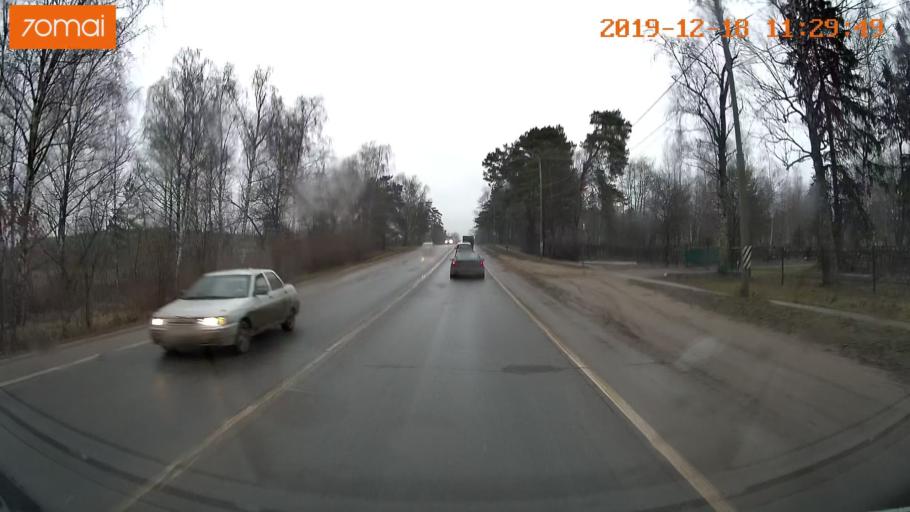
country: RU
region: Moskovskaya
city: Bol'shiye Vyazemy
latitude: 55.6522
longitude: 36.9704
